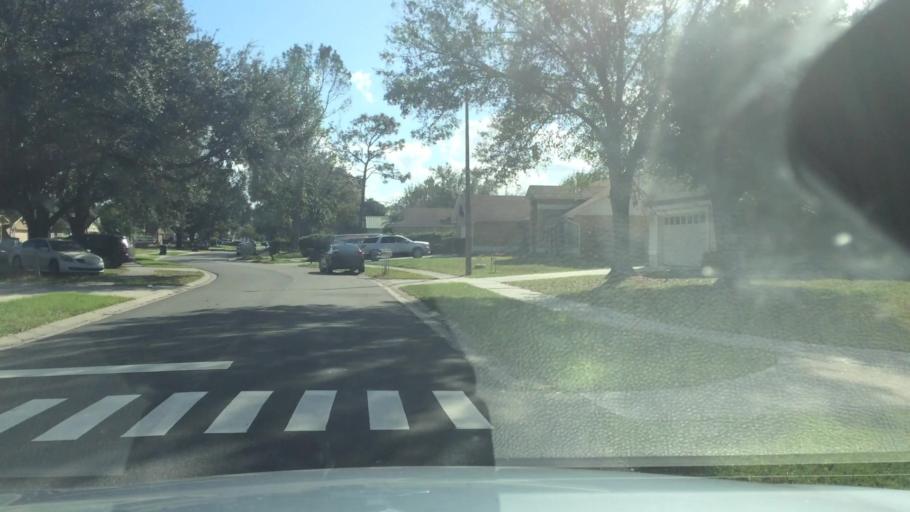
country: US
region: Florida
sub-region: Osceola County
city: Saint Cloud
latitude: 28.2133
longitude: -81.2844
